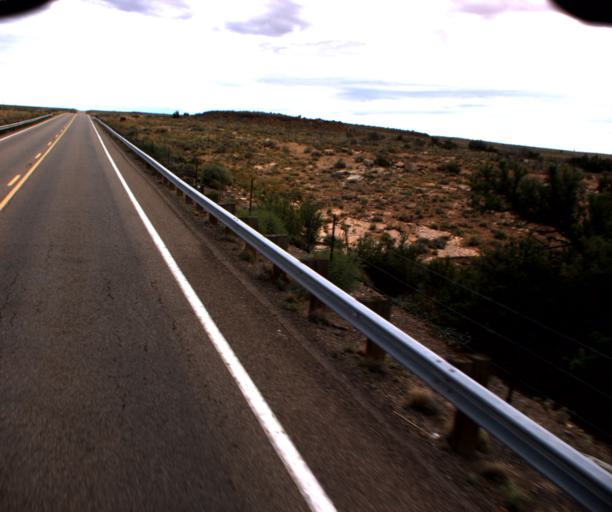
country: US
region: Arizona
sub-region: Navajo County
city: Holbrook
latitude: 34.8382
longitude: -110.1454
